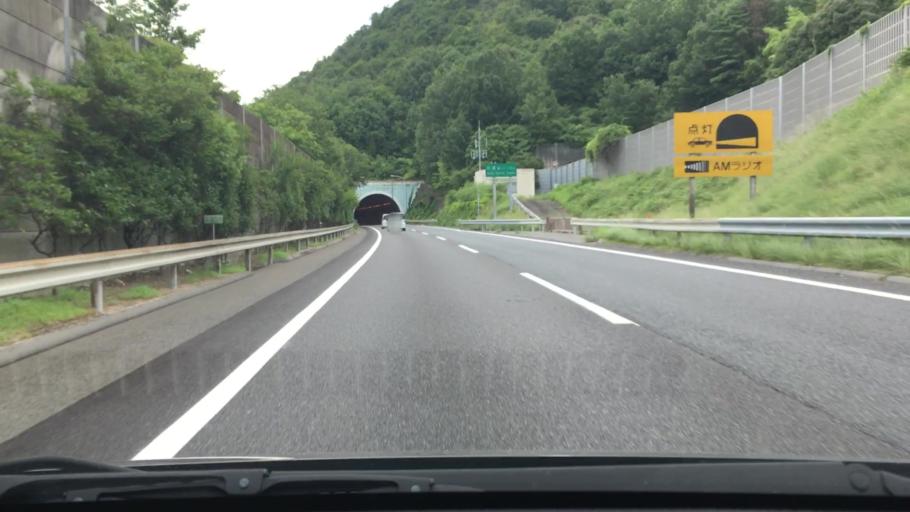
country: JP
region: Hiroshima
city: Ono-hara
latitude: 34.2629
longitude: 132.2313
